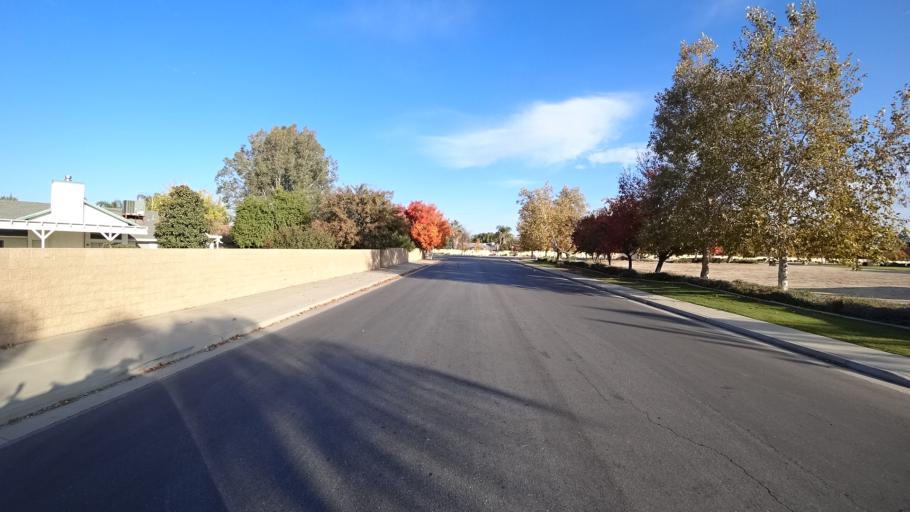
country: US
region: California
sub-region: Kern County
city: Rosedale
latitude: 35.3535
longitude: -119.1581
